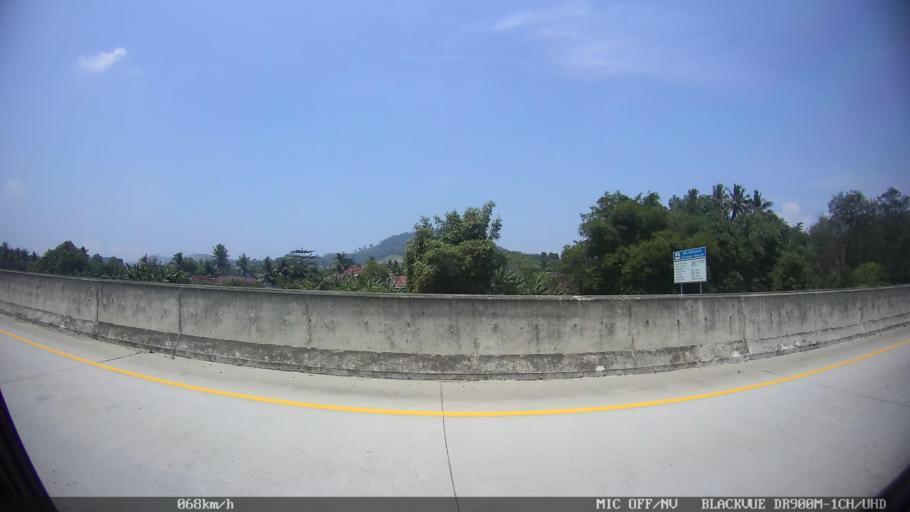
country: ID
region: Lampung
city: Kedaton
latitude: -5.3920
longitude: 105.3449
